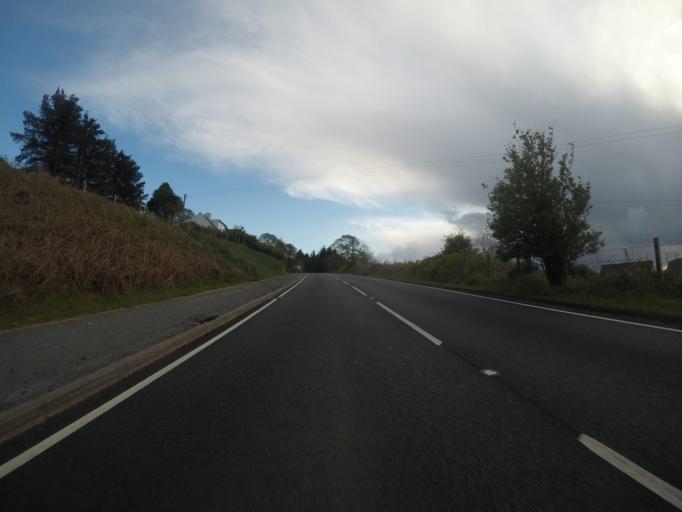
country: GB
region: Scotland
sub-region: Highland
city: Portree
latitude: 57.5874
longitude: -6.3562
